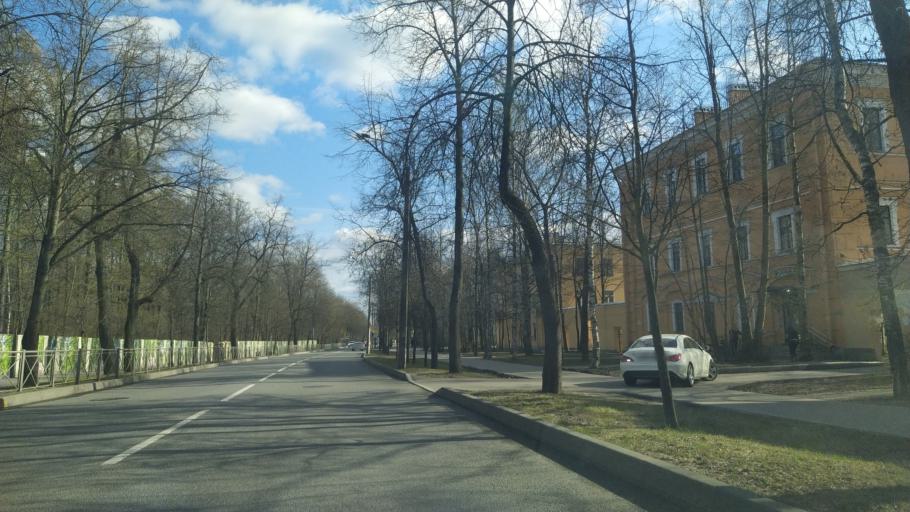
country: RU
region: St.-Petersburg
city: Pushkin
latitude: 59.7085
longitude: 30.4147
